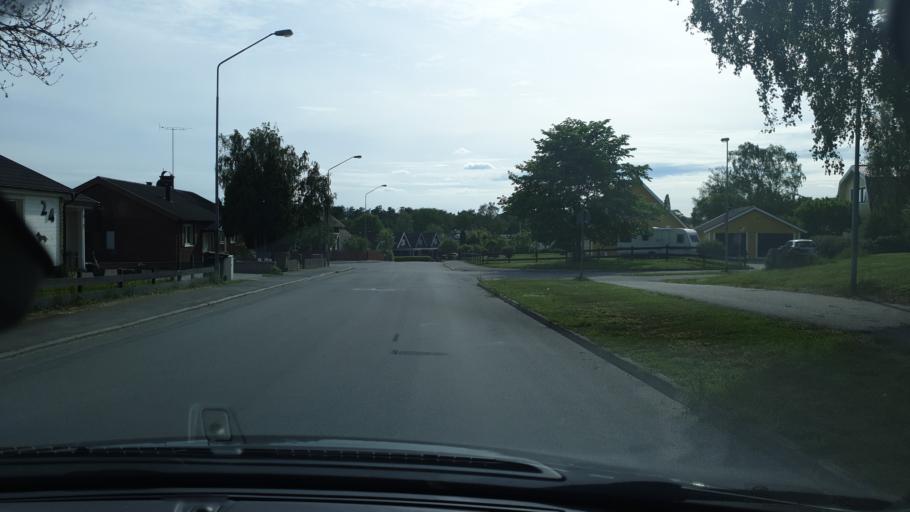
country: SE
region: Joenkoeping
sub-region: Vetlanda Kommun
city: Vetlanda
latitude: 57.4338
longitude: 15.0920
